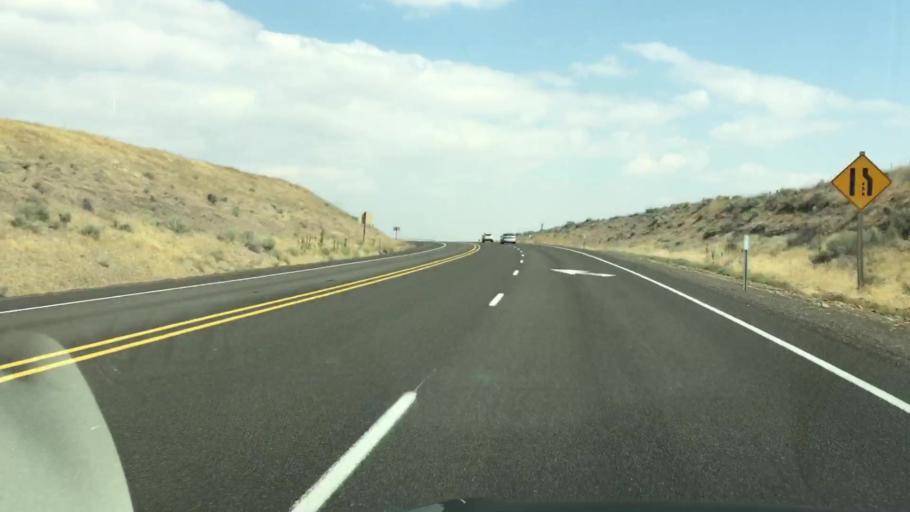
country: US
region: Oregon
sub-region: Wasco County
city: The Dalles
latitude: 45.4646
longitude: -121.1229
